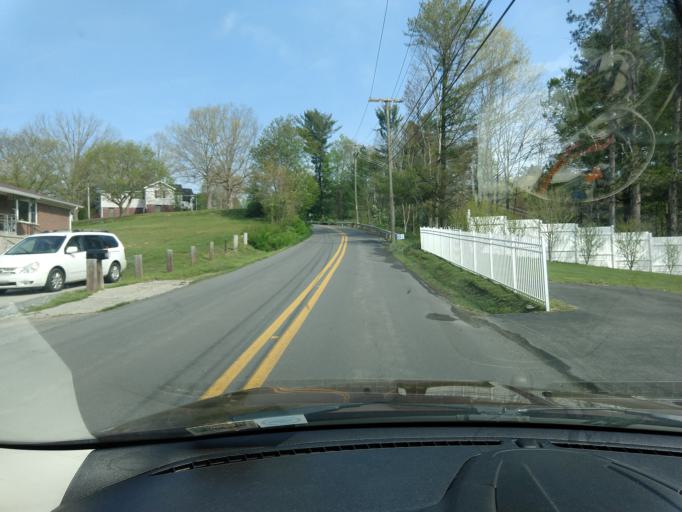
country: US
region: West Virginia
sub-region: Raleigh County
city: Crab Orchard
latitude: 37.7457
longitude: -81.2316
